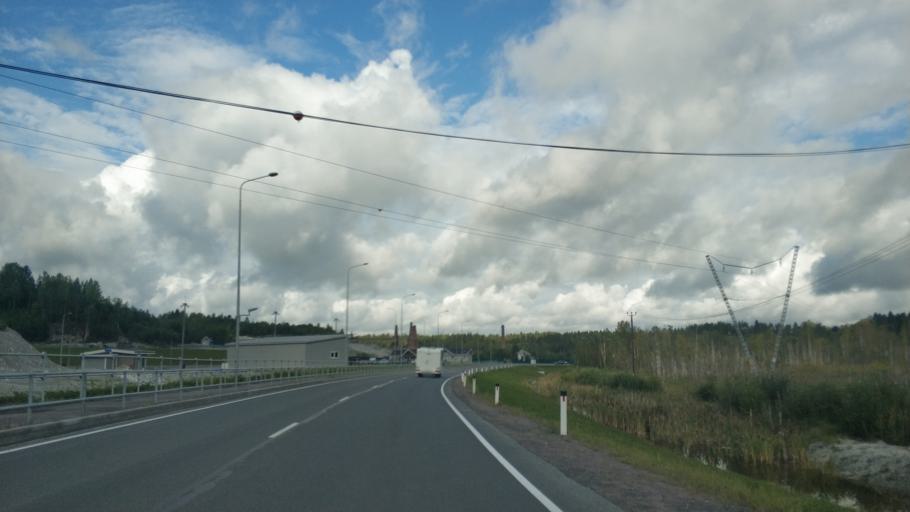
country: RU
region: Republic of Karelia
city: Ruskeala
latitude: 61.9479
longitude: 30.5889
